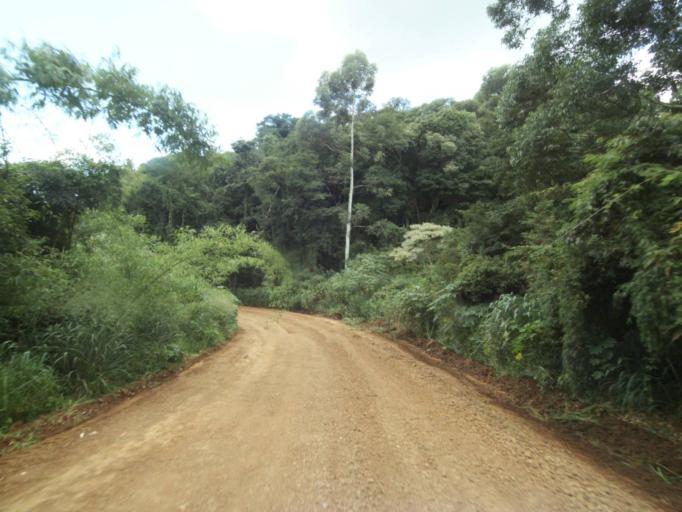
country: BR
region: Parana
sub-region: Guaraniacu
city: Guaraniacu
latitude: -25.1036
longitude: -52.8590
